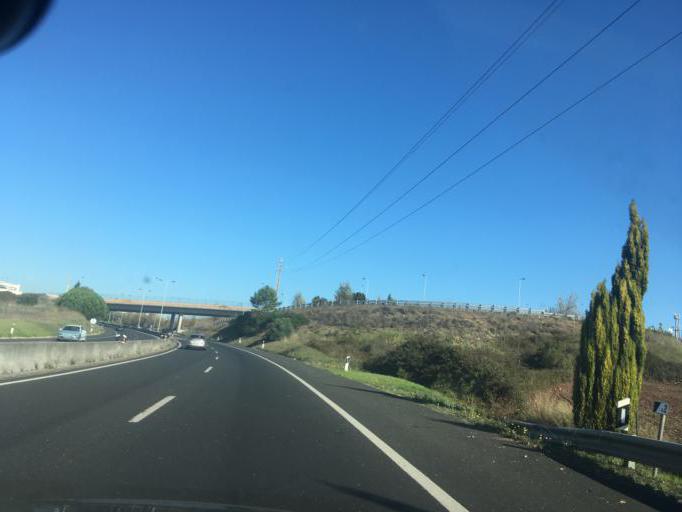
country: PT
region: Lisbon
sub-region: Oeiras
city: Porto Salvo
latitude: 38.7296
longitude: -9.2959
